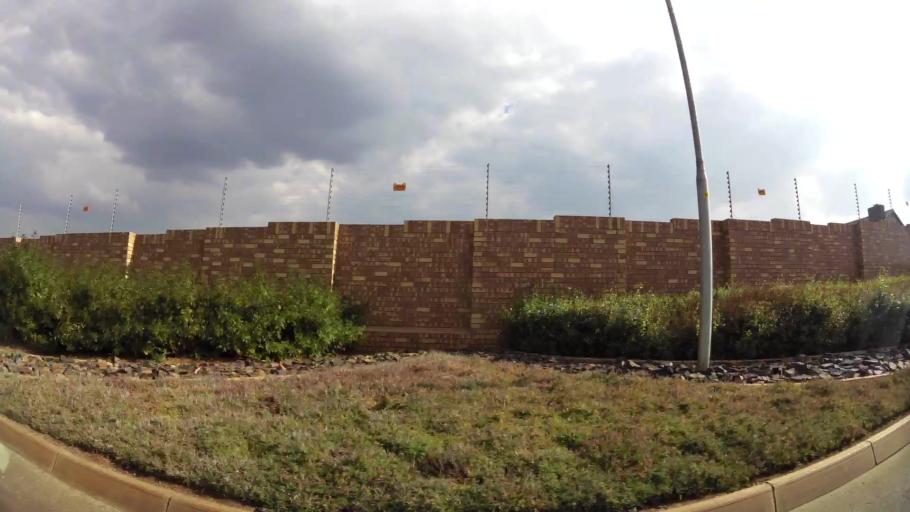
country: ZA
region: Gauteng
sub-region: Ekurhuleni Metropolitan Municipality
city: Tembisa
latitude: -25.9350
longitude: 28.2052
